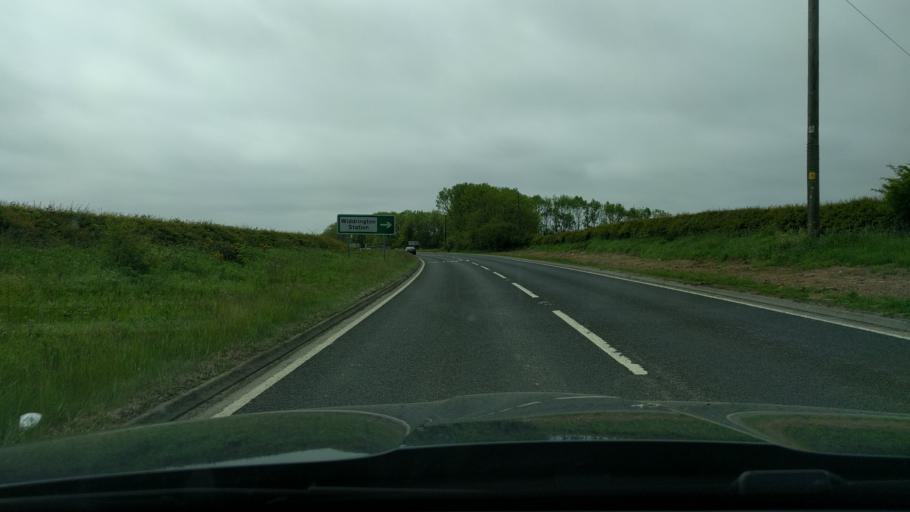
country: GB
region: England
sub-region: Northumberland
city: Cresswell
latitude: 55.2367
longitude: -1.5925
